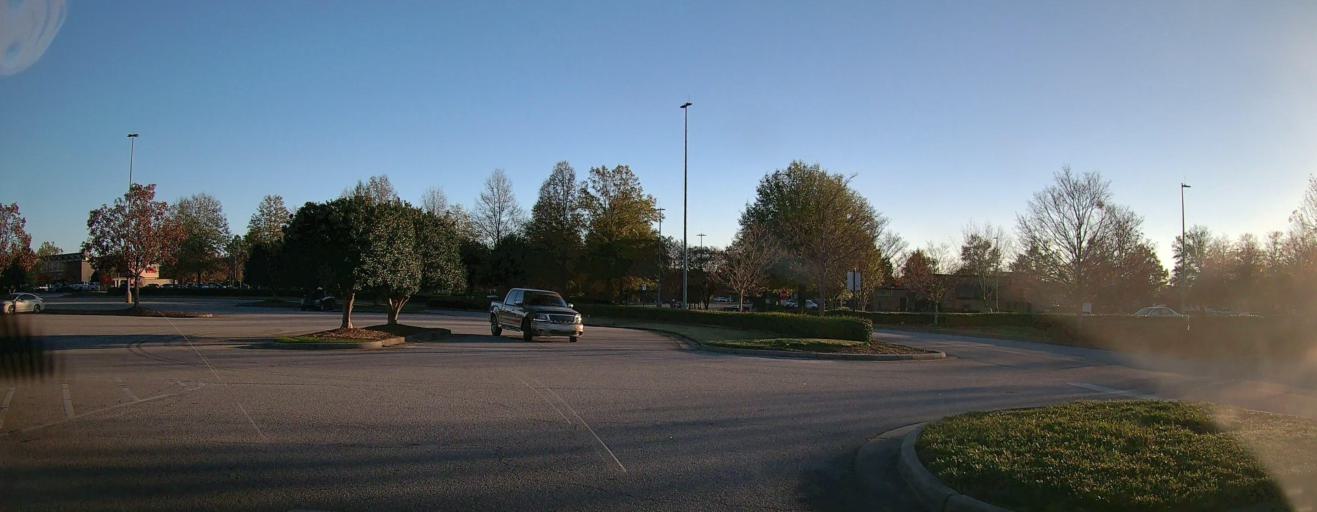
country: US
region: Georgia
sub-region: Gwinnett County
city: Buford
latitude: 34.0633
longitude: -83.9881
